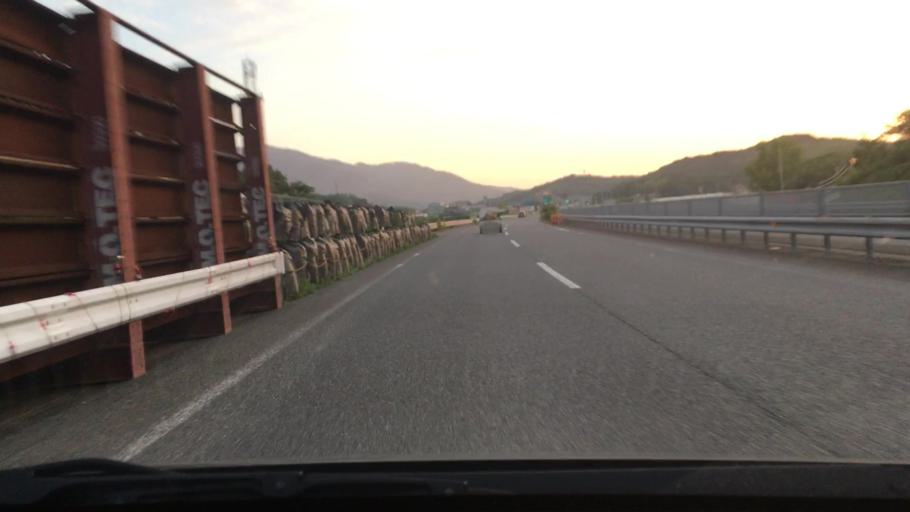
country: JP
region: Fukuoka
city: Maebaru-chuo
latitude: 33.5322
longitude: 130.1895
